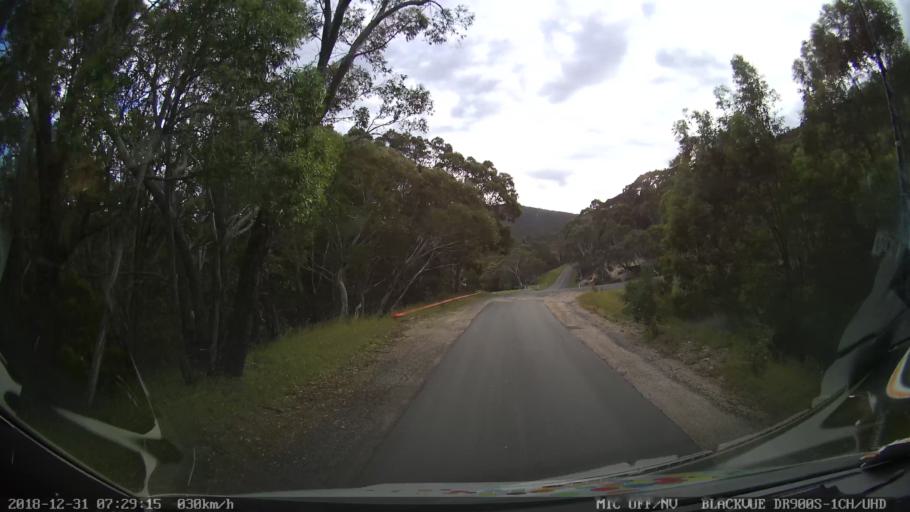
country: AU
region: New South Wales
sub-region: Snowy River
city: Jindabyne
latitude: -36.3231
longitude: 148.4773
